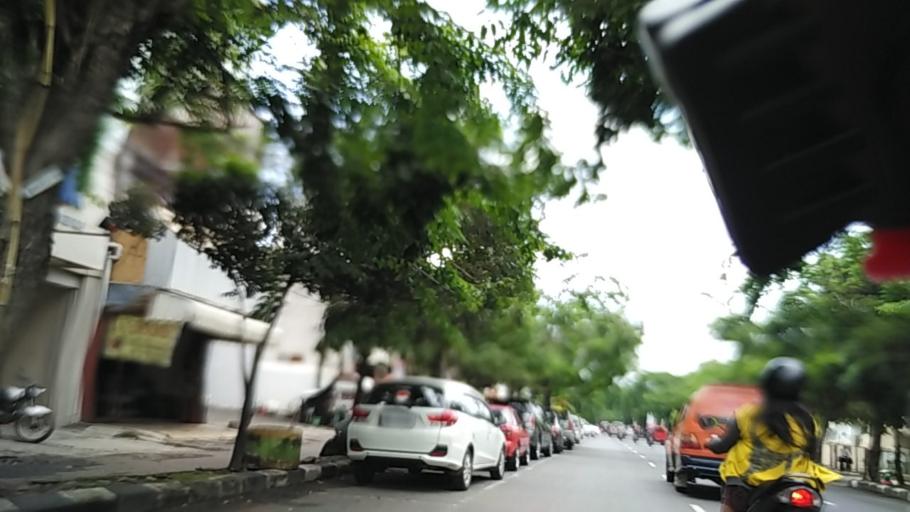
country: ID
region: Central Java
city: Semarang
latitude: -6.9908
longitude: 110.4319
